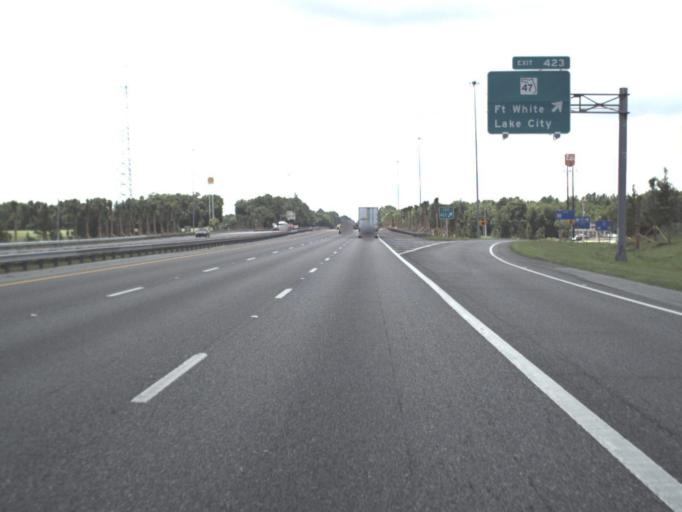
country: US
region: Florida
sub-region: Columbia County
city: Lake City
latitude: 30.1198
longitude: -82.6572
